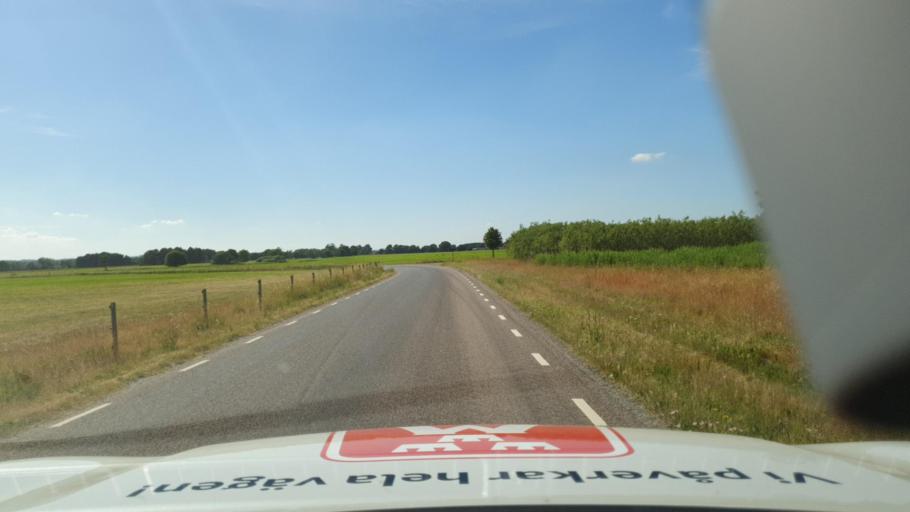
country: SE
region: Skane
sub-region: Sjobo Kommun
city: Blentarp
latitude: 55.6201
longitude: 13.6463
